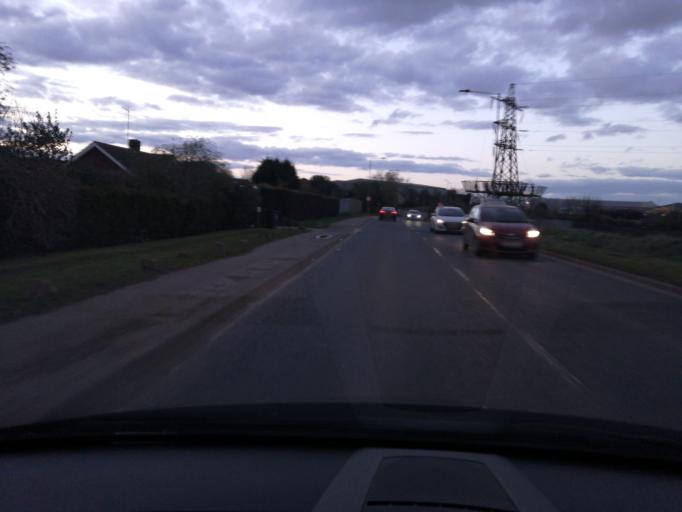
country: GB
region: England
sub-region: Peterborough
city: Eye
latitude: 52.5874
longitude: -0.2038
